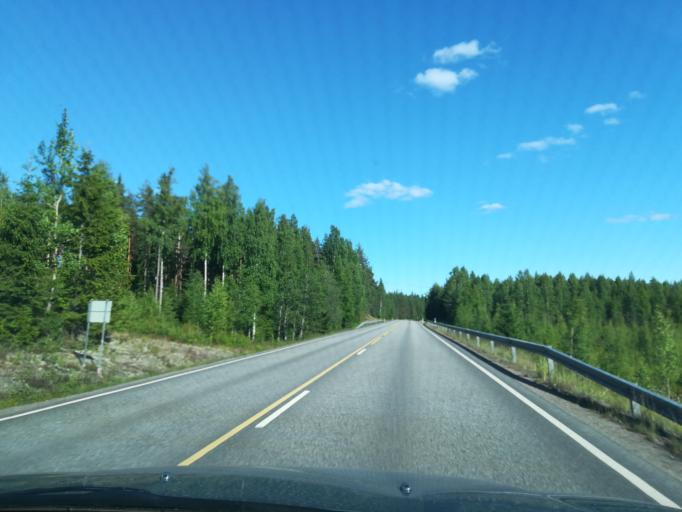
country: FI
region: South Karelia
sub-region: Imatra
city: Ruokolahti
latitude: 61.3909
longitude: 28.6420
